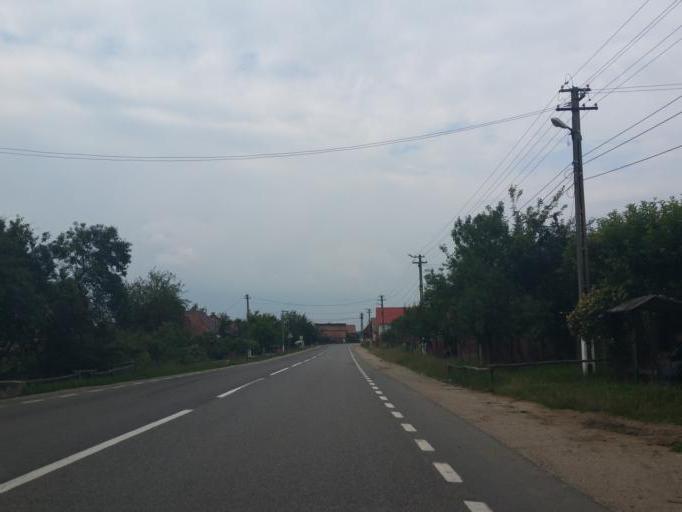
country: RO
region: Salaj
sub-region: Comuna Romanasi
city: Romanasi
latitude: 47.0838
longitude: 23.1895
